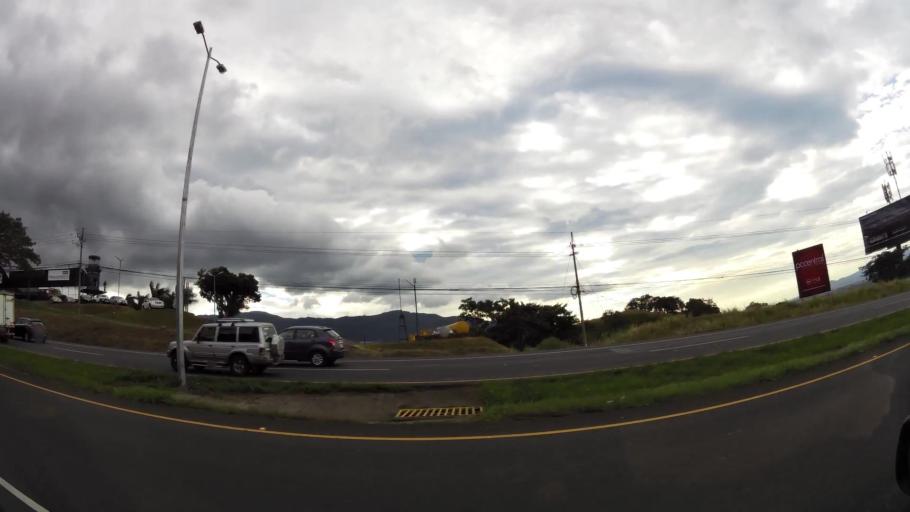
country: CR
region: San Jose
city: Santa Ana
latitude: 9.9447
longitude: -84.1728
